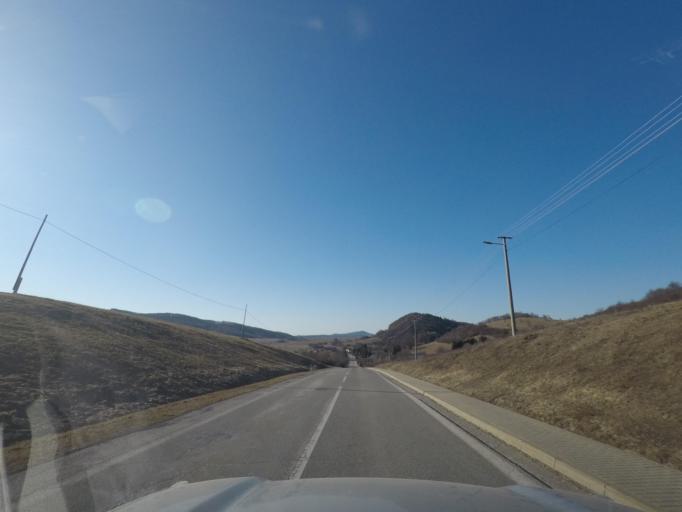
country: SK
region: Presovsky
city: Medzilaborce
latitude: 49.2240
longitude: 21.9716
